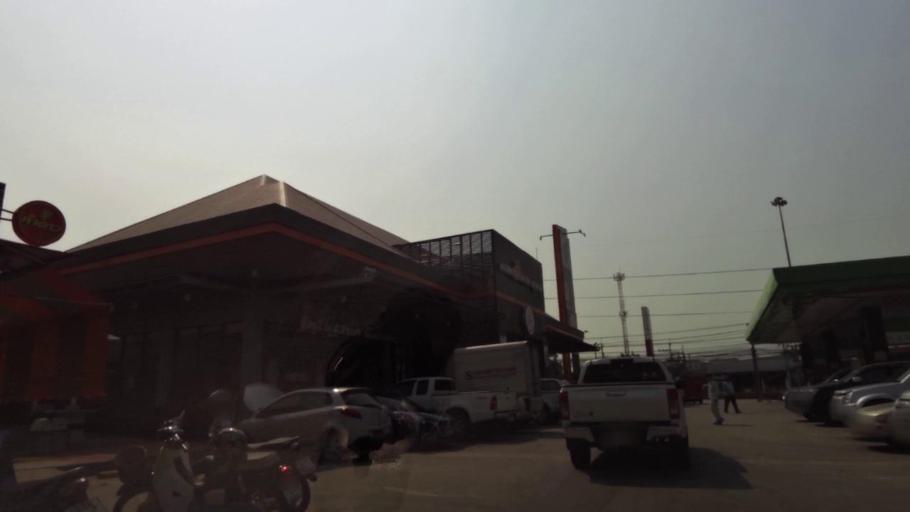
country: TH
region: Chon Buri
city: Chon Buri
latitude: 13.4136
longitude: 101.0001
